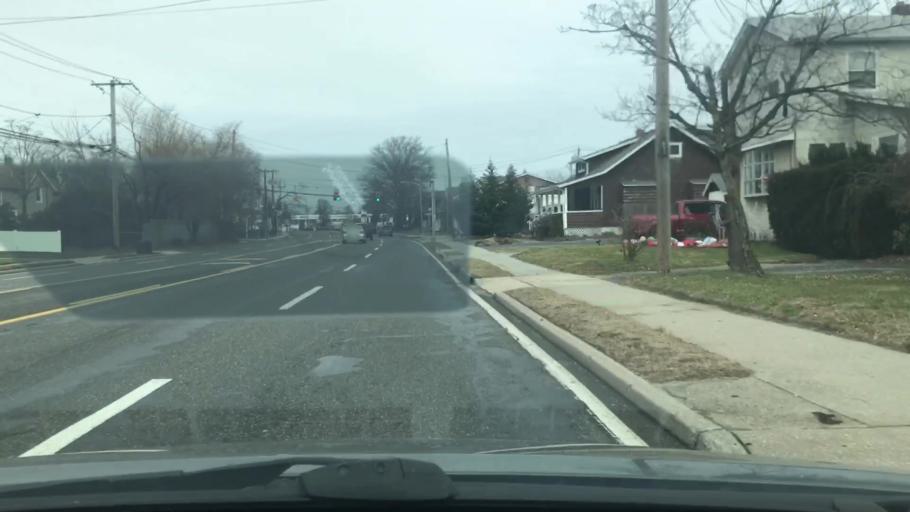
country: US
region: New York
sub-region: Suffolk County
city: Babylon
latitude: 40.6994
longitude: -73.3425
